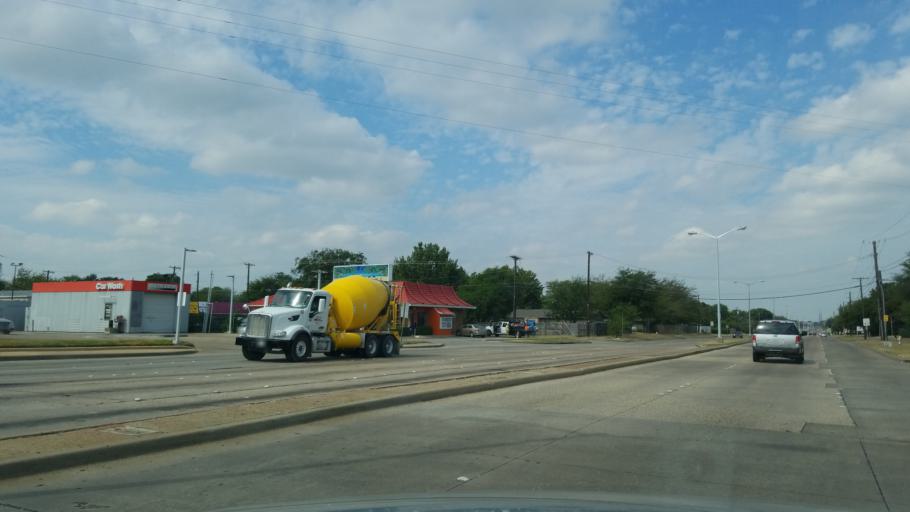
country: US
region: Texas
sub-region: Dallas County
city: Garland
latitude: 32.9094
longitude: -96.6829
